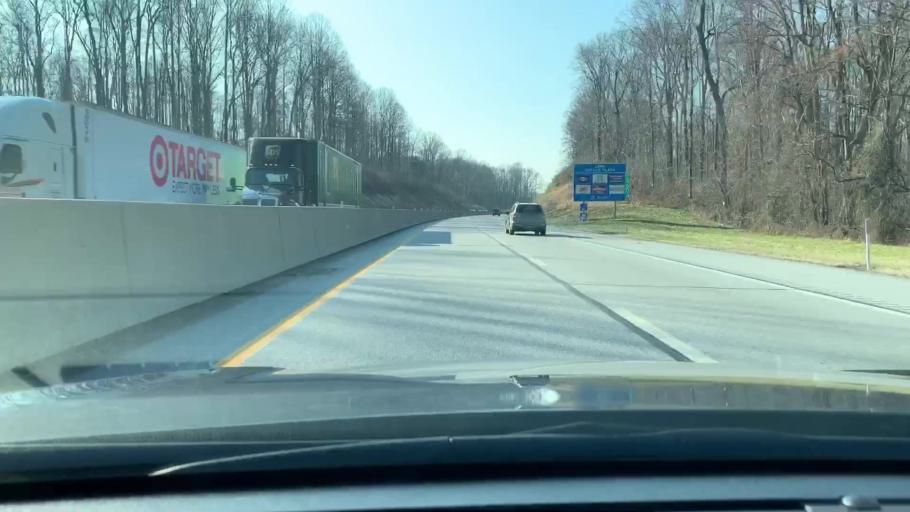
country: US
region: Pennsylvania
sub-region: Lebanon County
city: Campbelltown
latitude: 40.2138
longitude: -76.5352
